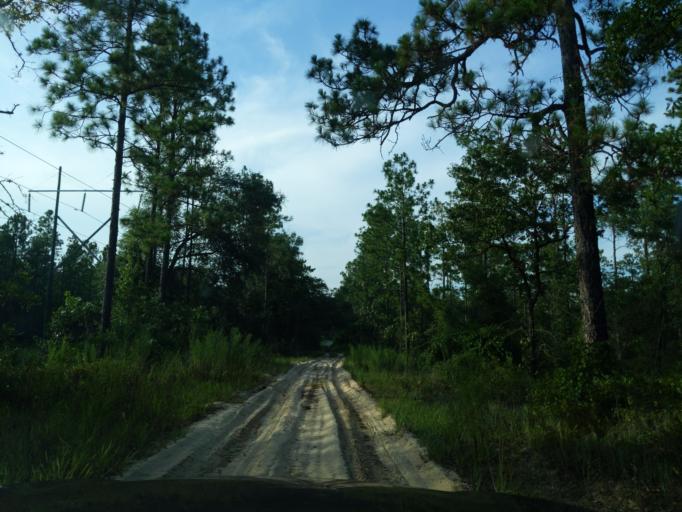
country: US
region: Florida
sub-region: Leon County
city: Tallahassee
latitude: 30.3646
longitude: -84.3611
